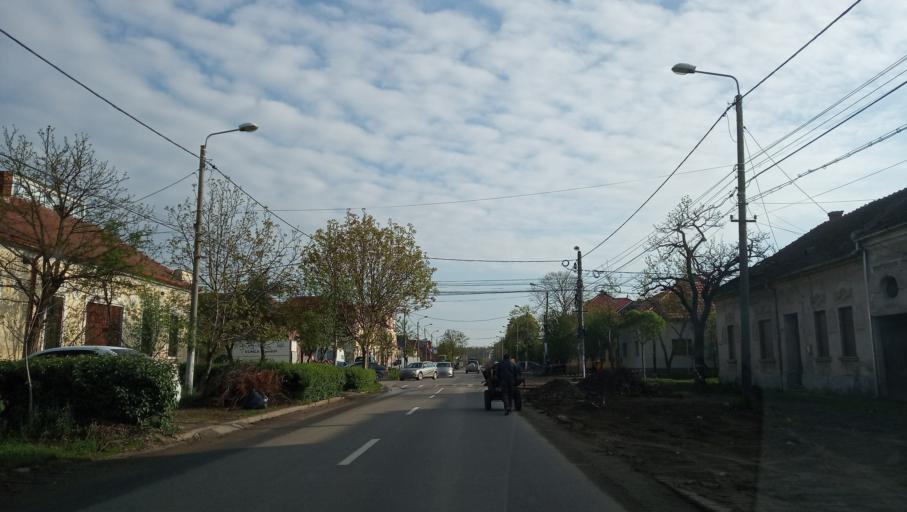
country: RO
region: Timis
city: Timisoara
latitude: 45.7615
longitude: 21.2611
